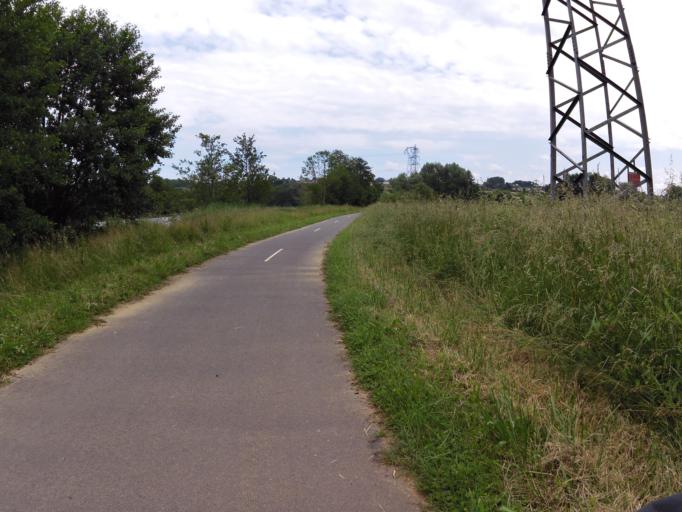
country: FR
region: Champagne-Ardenne
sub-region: Departement des Ardennes
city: Lumes
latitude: 49.7412
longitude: 4.7761
